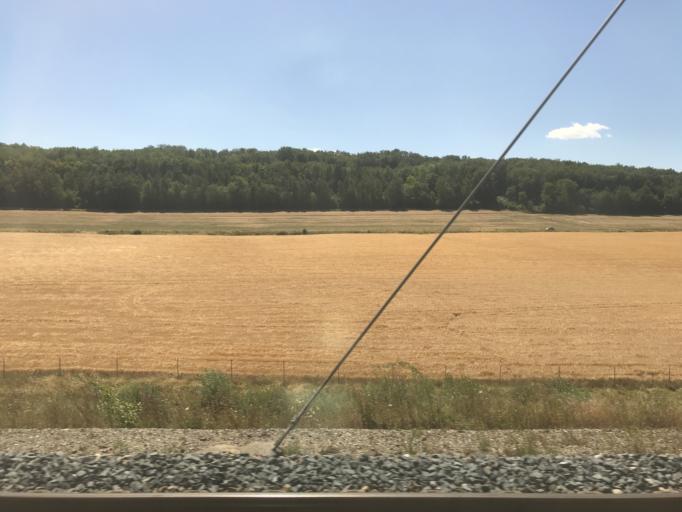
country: FR
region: Lorraine
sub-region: Departement de la Meuse
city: Dugny-sur-Meuse
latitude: 48.9800
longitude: 5.2550
